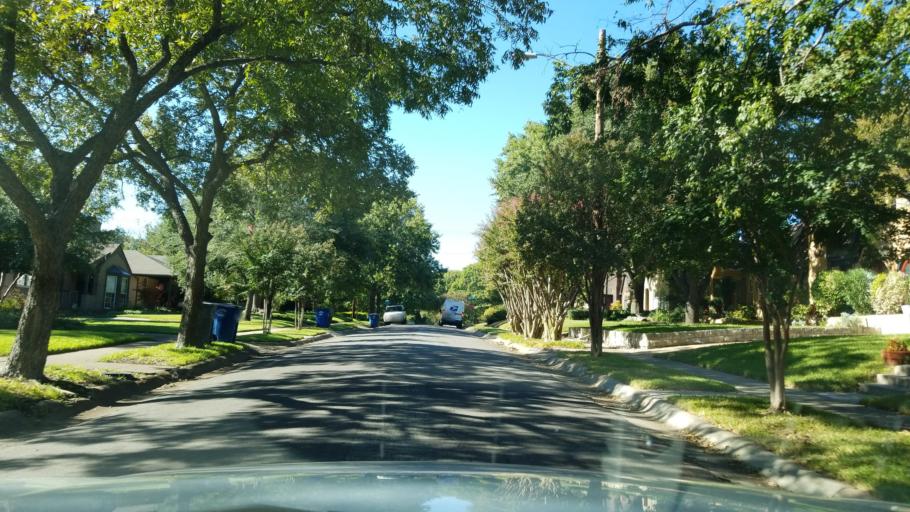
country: US
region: Texas
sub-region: Dallas County
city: Highland Park
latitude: 32.8028
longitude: -96.7424
